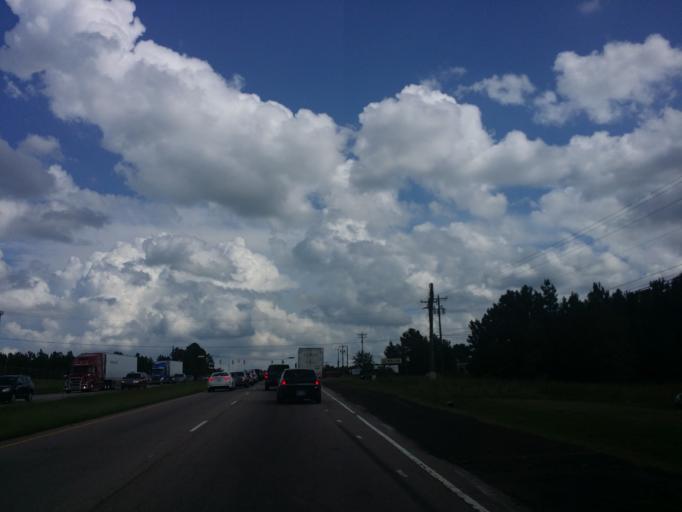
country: US
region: North Carolina
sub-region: Durham County
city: Gorman
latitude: 35.9334
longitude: -78.8111
